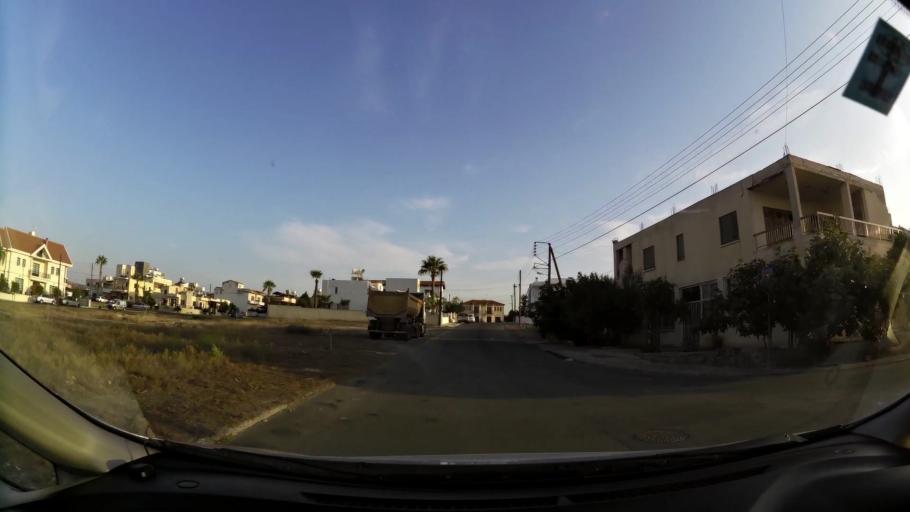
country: CY
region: Larnaka
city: Aradippou
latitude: 34.9226
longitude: 33.5903
